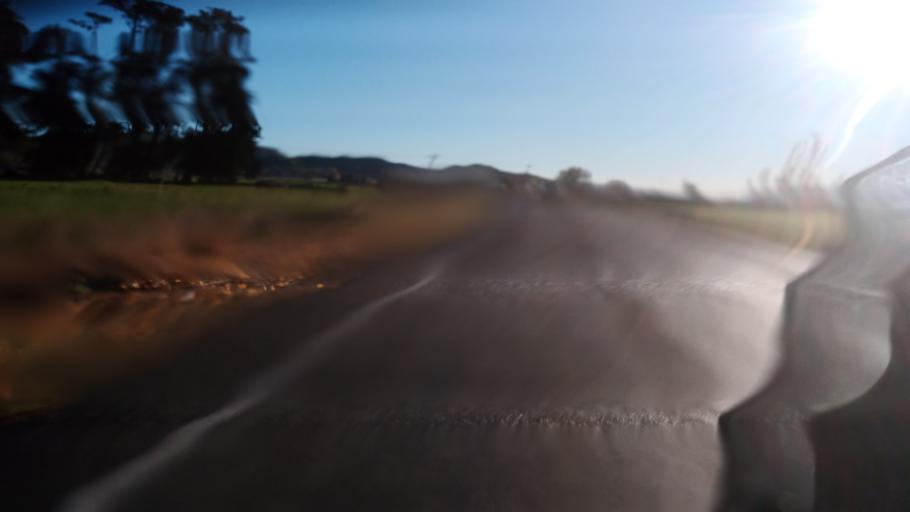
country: NZ
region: Hawke's Bay
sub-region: Wairoa District
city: Wairoa
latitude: -39.0254
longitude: 177.3745
